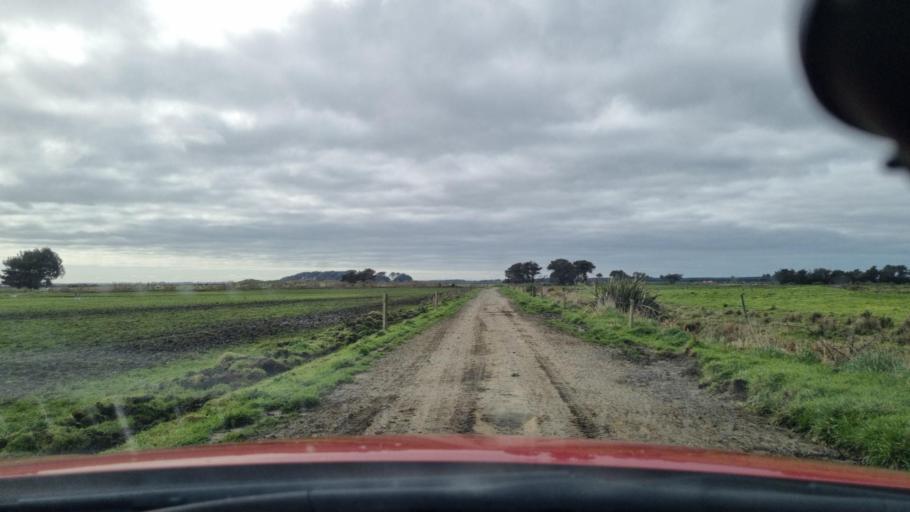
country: NZ
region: Southland
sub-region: Invercargill City
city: Bluff
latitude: -46.5154
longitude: 168.3040
